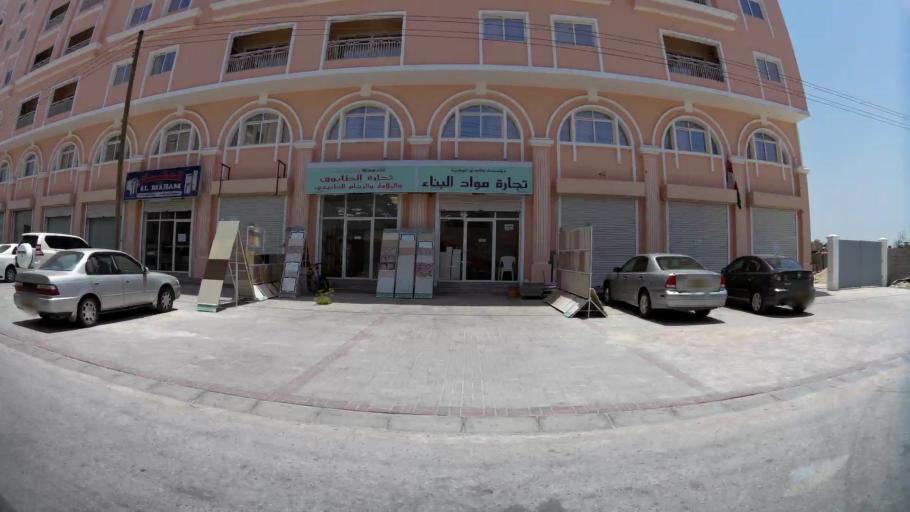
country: OM
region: Zufar
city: Salalah
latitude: 17.0208
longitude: 54.1127
